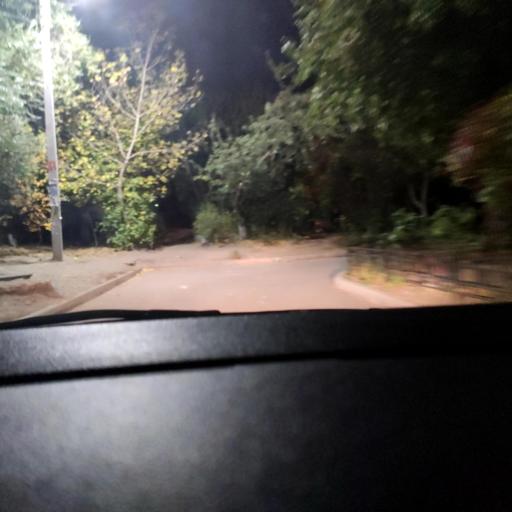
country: RU
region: Voronezj
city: Voronezh
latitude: 51.6771
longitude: 39.1326
